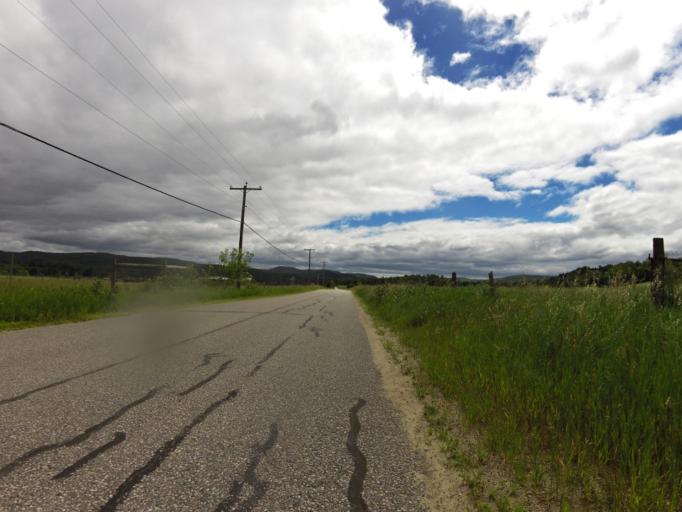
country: CA
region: Quebec
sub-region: Laurentides
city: Mont-Tremblant
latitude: 45.9576
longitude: -74.6013
